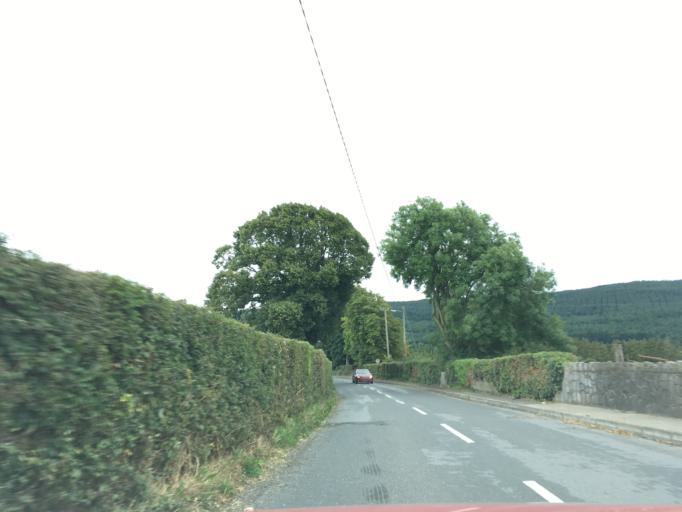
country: IE
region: Munster
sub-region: South Tipperary
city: Cluain Meala
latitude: 52.3664
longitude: -7.5843
